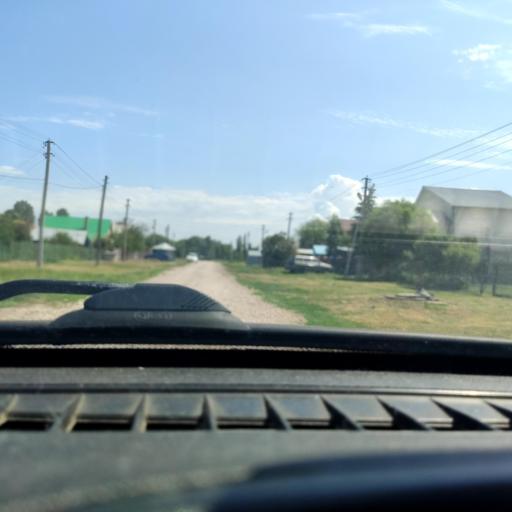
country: RU
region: Samara
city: Tol'yatti
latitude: 53.6358
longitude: 49.2950
